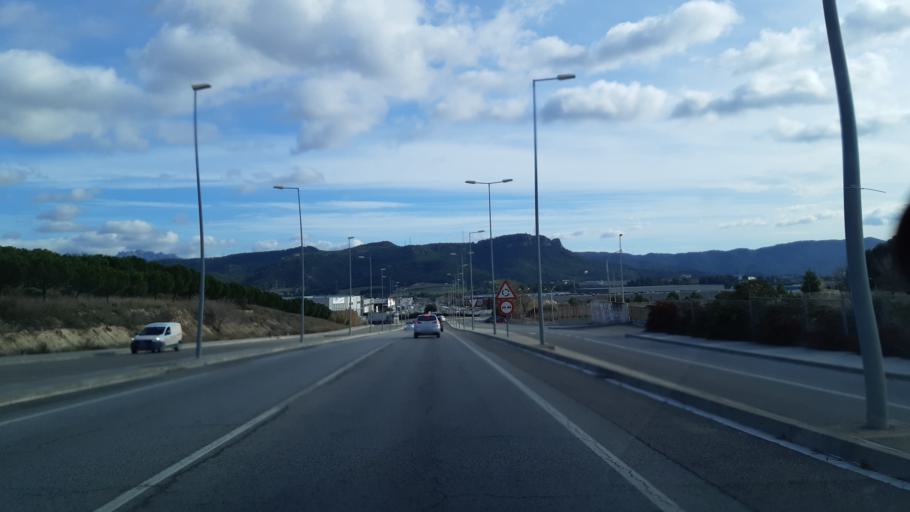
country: ES
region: Catalonia
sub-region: Provincia de Barcelona
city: Vilanova del Cami
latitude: 41.5783
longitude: 1.6466
